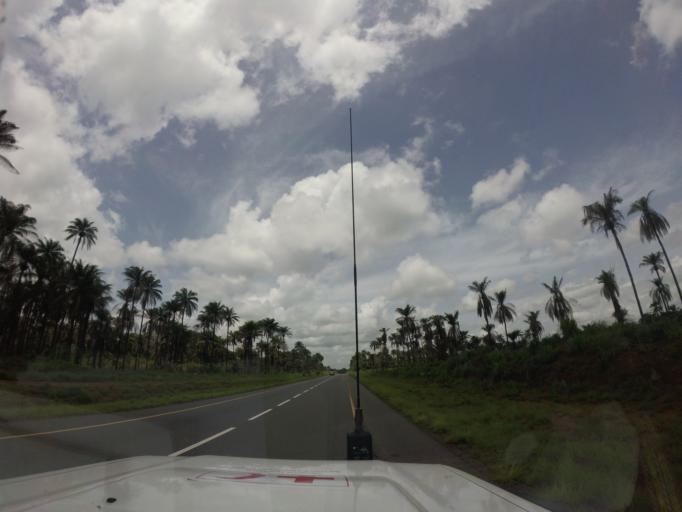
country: SL
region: Northern Province
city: Mange
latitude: 8.8868
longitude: -12.8355
